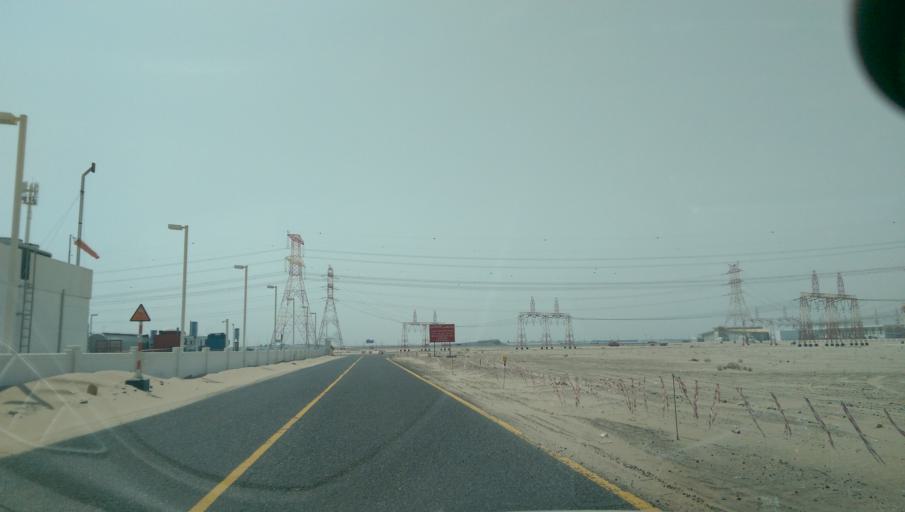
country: AE
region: Abu Dhabi
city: Abu Dhabi
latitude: 24.2965
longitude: 54.5400
